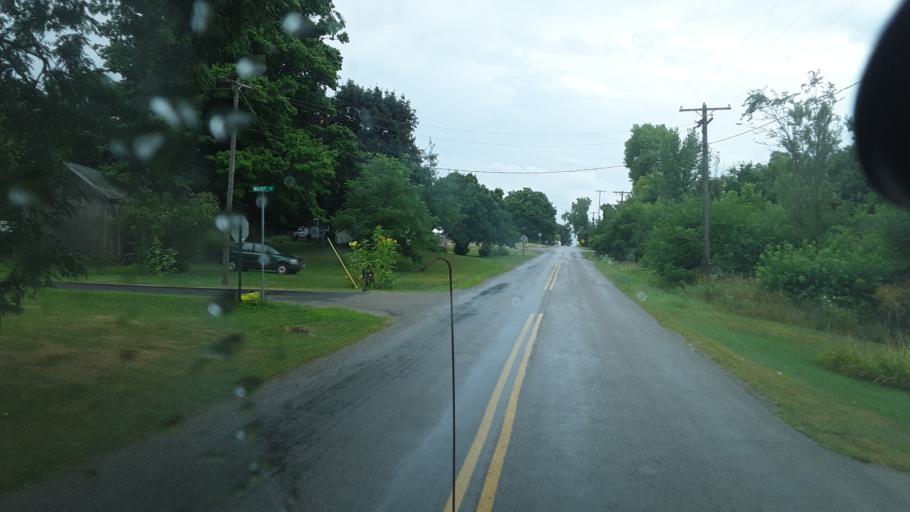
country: US
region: Indiana
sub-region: Steuben County
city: Hamilton
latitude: 41.6344
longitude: -84.7890
